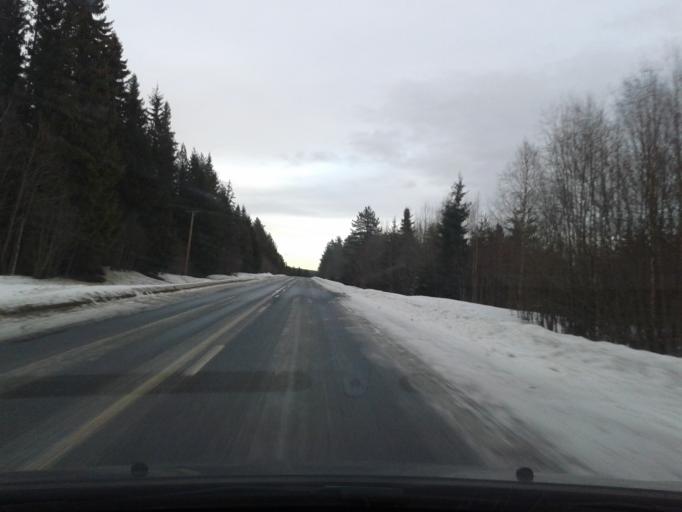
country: SE
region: Vaesternorrland
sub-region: Solleftea Kommun
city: Solleftea
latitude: 63.3326
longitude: 17.1039
